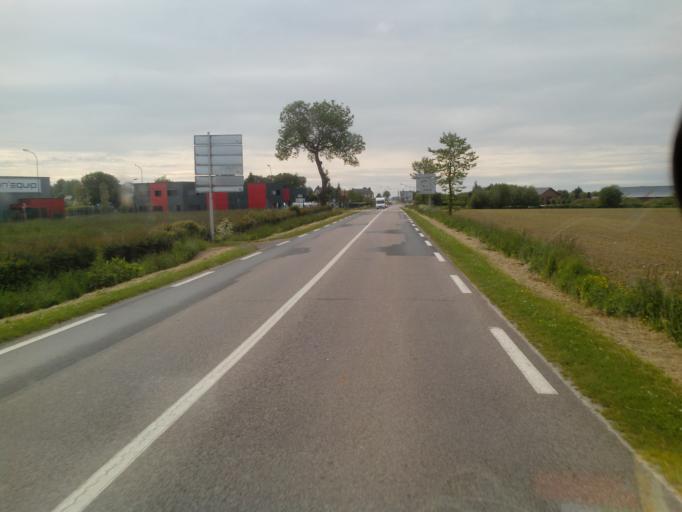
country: FR
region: Haute-Normandie
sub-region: Departement de la Seine-Maritime
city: Fauville-en-Caux
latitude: 49.6567
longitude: 0.5965
